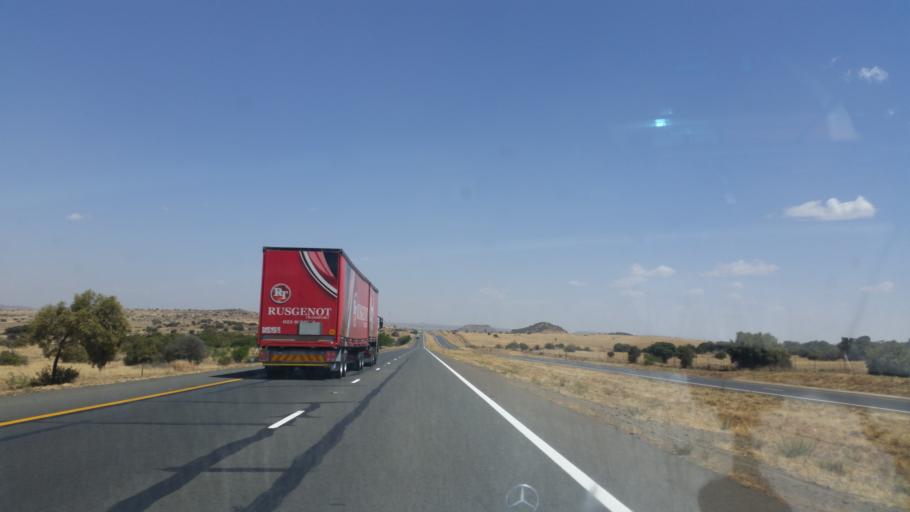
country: ZA
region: Orange Free State
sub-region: Lejweleputswa District Municipality
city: Brandfort
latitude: -28.9202
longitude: 26.4419
